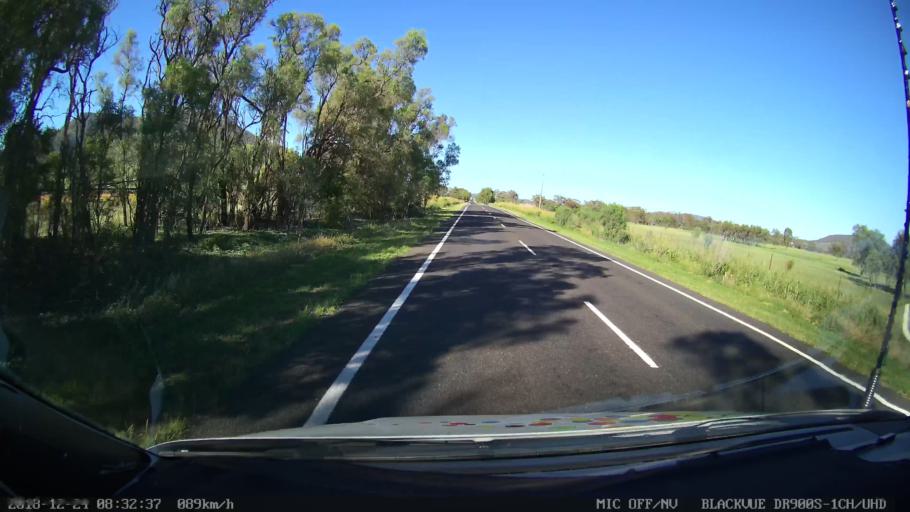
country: AU
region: New South Wales
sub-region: Tamworth Municipality
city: Phillip
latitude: -31.2811
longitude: 150.6956
